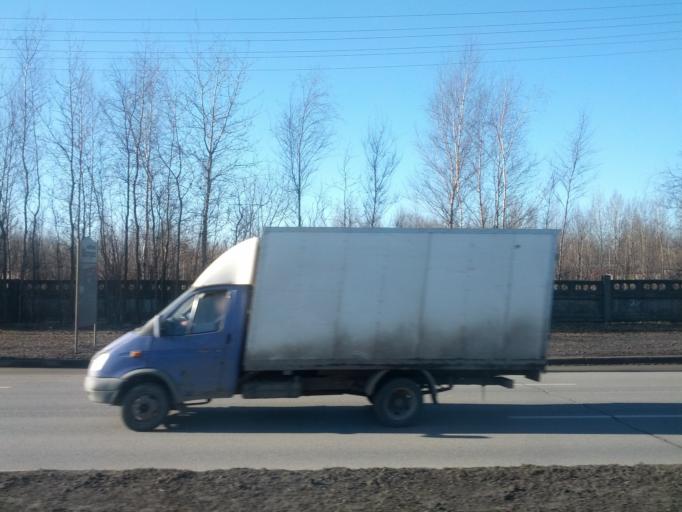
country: RU
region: St.-Petersburg
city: Obukhovo
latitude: 59.9113
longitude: 30.4416
